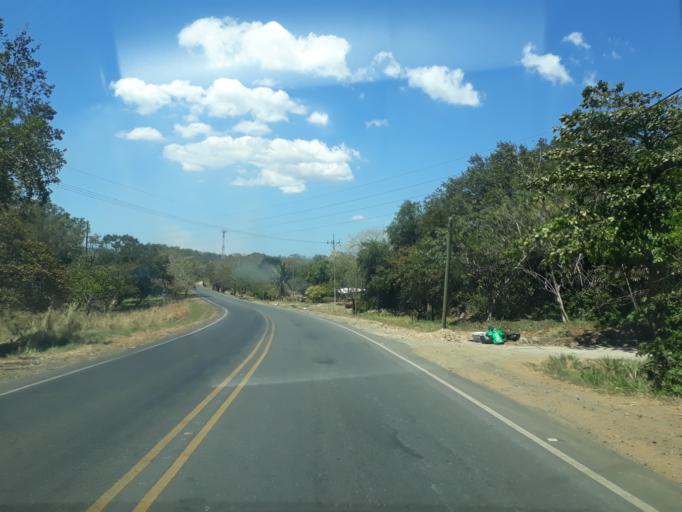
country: CR
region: Guanacaste
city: Liberia
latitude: 10.6666
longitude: -85.4746
